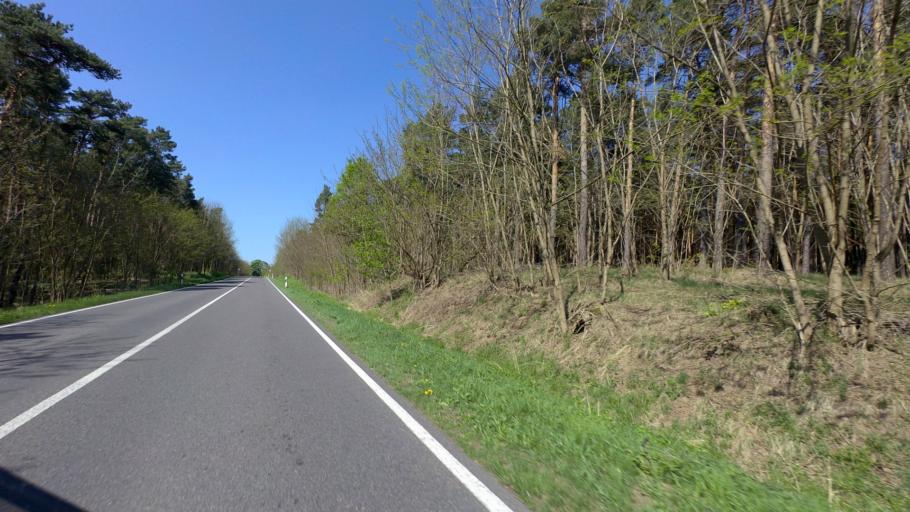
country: DE
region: Brandenburg
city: Lieberose
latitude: 52.0343
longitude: 14.2978
